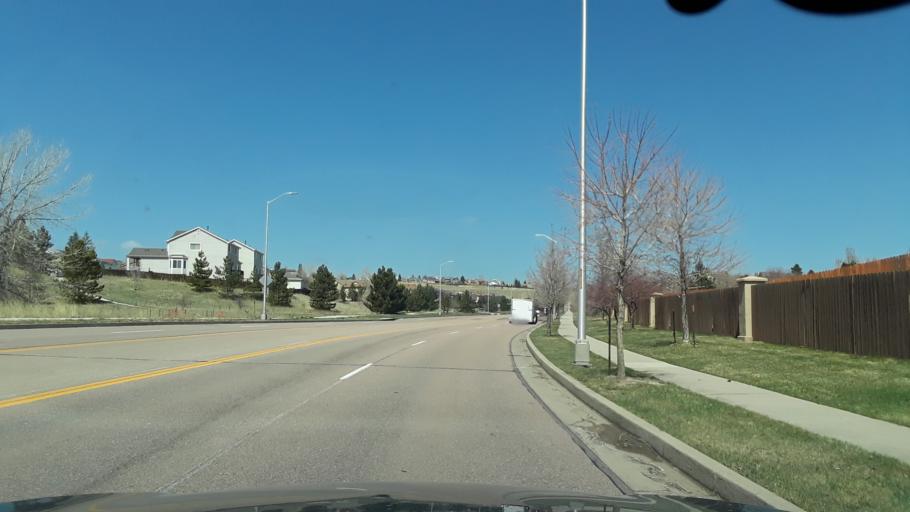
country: US
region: Colorado
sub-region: El Paso County
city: Black Forest
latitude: 38.9433
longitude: -104.7417
